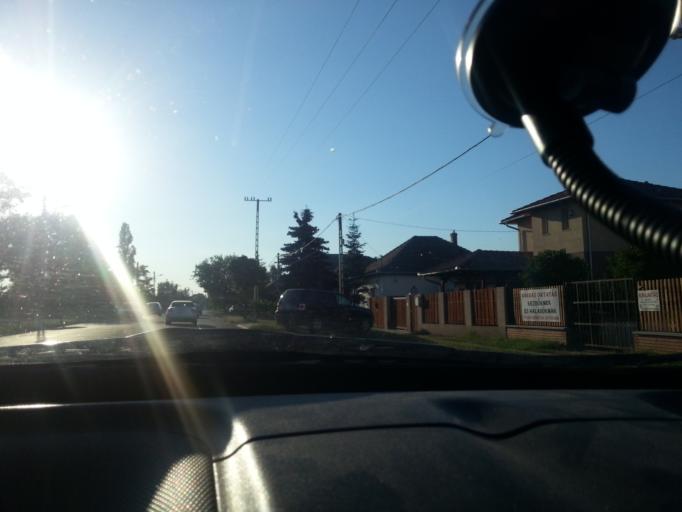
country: HU
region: Pest
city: Gyal
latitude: 47.4251
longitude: 19.2293
